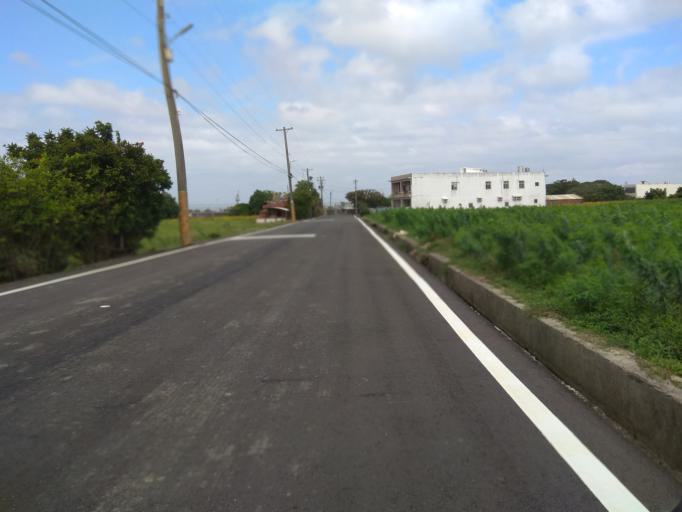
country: TW
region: Taiwan
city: Taoyuan City
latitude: 25.0626
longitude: 121.2309
